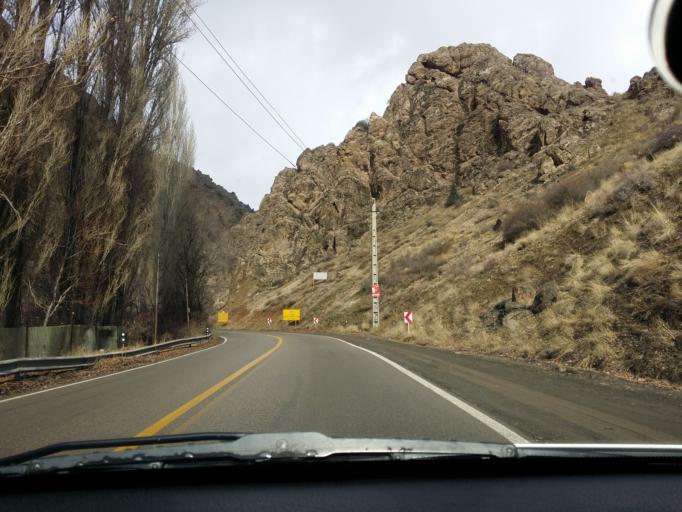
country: IR
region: Tehran
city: Tajrish
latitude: 36.0425
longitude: 51.3114
